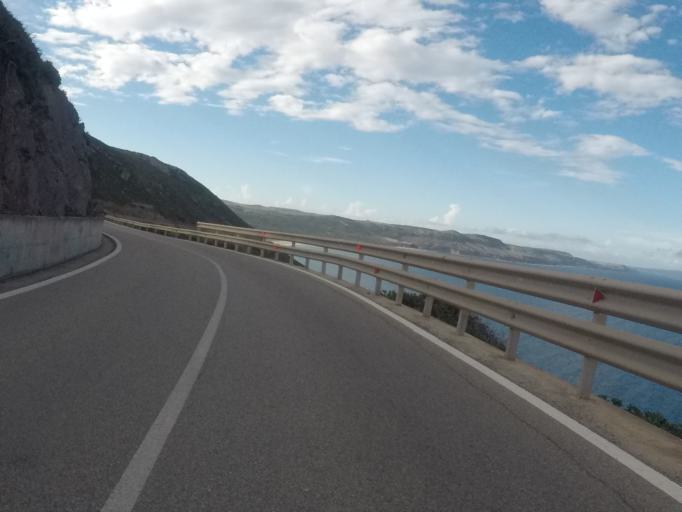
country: IT
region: Sardinia
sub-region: Provincia di Carbonia-Iglesias
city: Gonnesa
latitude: 39.3060
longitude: 8.4354
